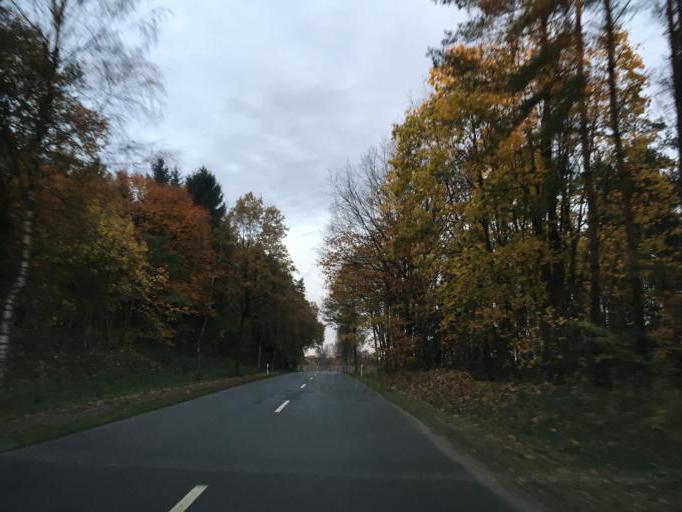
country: DE
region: Lower Saxony
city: Bispingen
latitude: 53.0736
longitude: 9.9744
